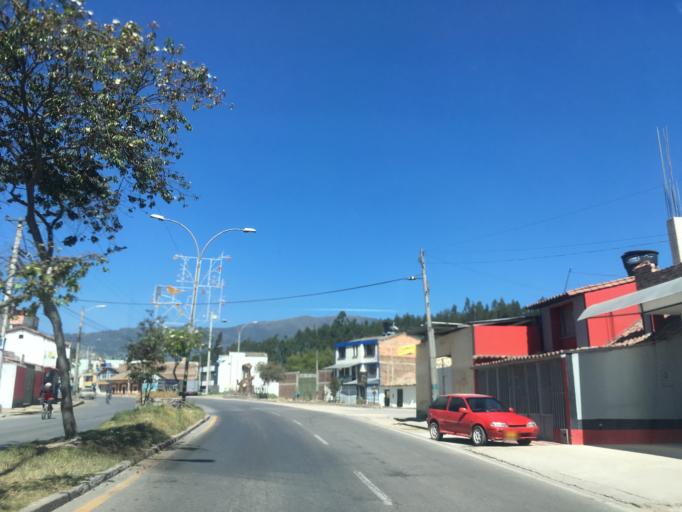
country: CO
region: Boyaca
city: Duitama
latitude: 5.8159
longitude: -73.0193
